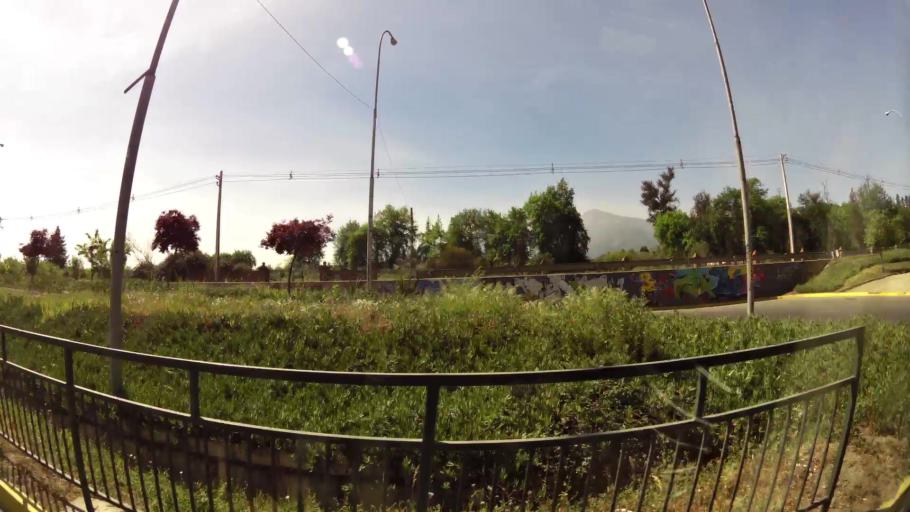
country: CL
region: Santiago Metropolitan
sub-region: Provincia de Cordillera
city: Puente Alto
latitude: -33.5961
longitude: -70.5349
